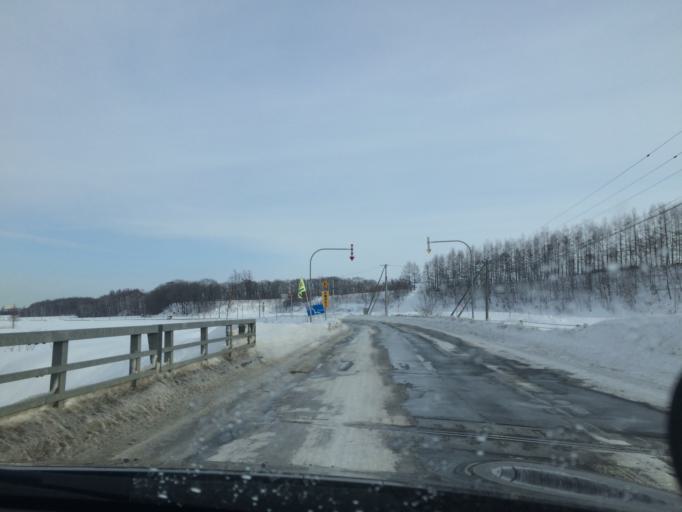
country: JP
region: Hokkaido
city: Obihiro
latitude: 42.9027
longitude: 143.0107
